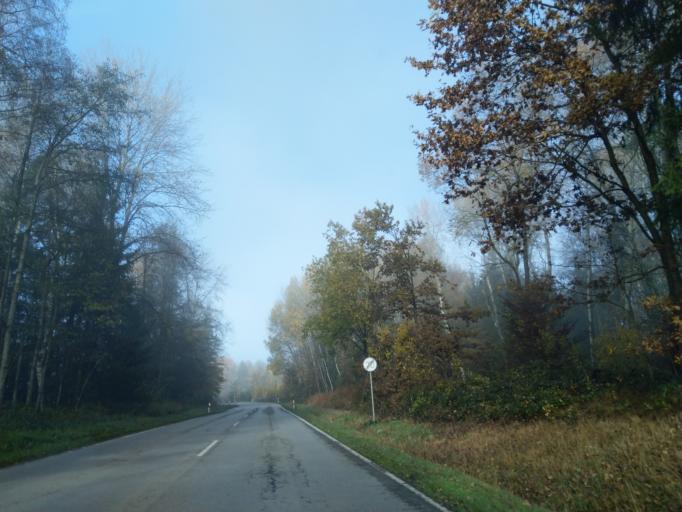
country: DE
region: Bavaria
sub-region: Lower Bavaria
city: Aussernzell
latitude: 48.7220
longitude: 13.2310
